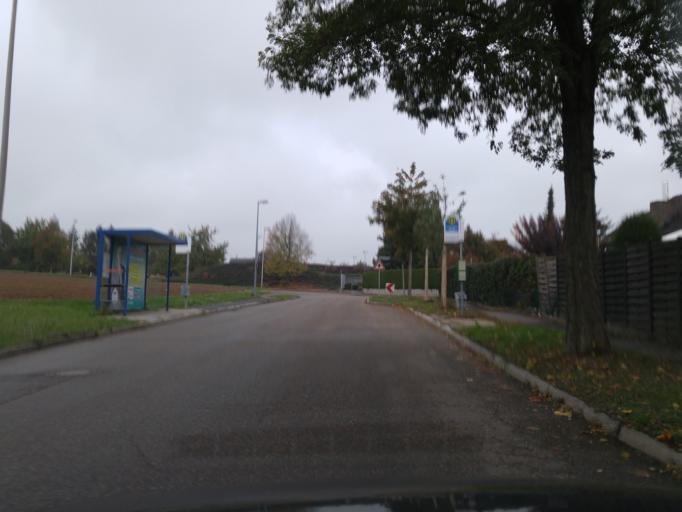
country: DE
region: Baden-Wuerttemberg
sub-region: Regierungsbezirk Stuttgart
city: Bad Wimpfen
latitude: 49.1990
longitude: 9.1479
